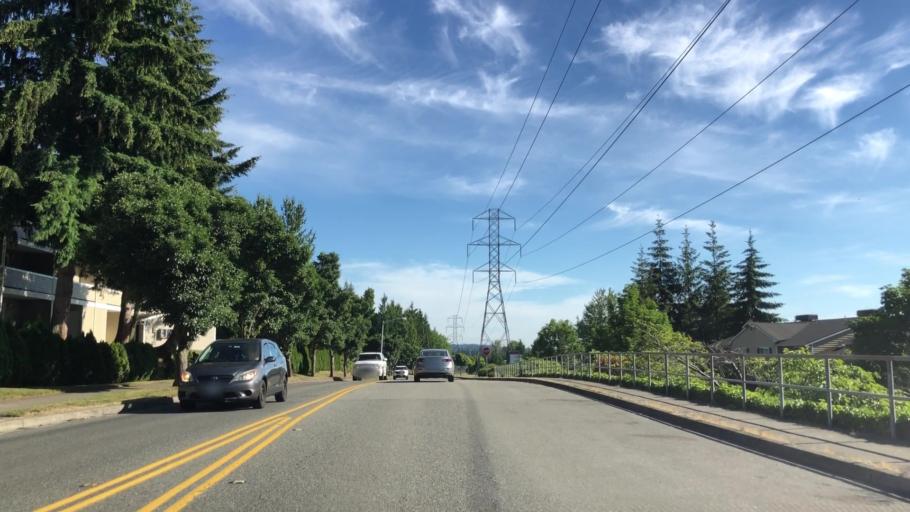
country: US
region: Washington
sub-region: King County
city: Kingsgate
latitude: 47.7178
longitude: -122.1755
